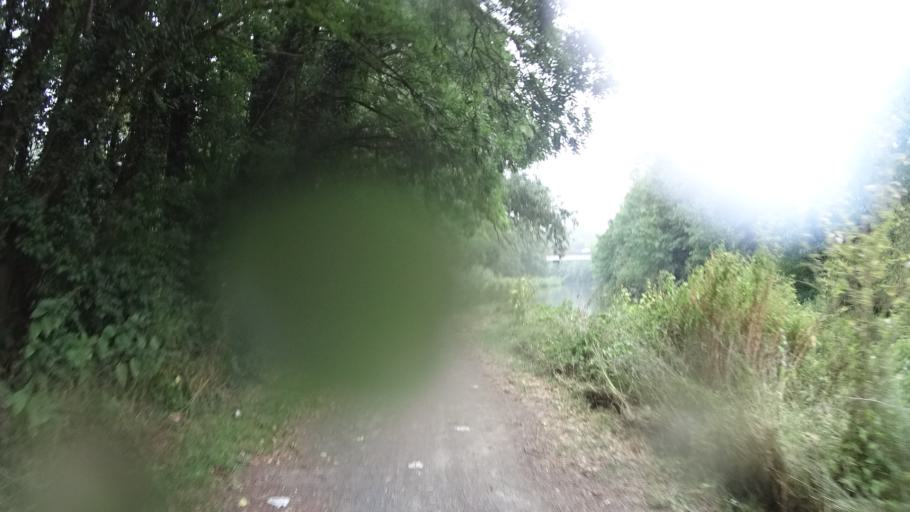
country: FR
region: Nord-Pas-de-Calais
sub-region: Departement du Nord
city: Louvroil
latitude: 50.2637
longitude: 3.9502
